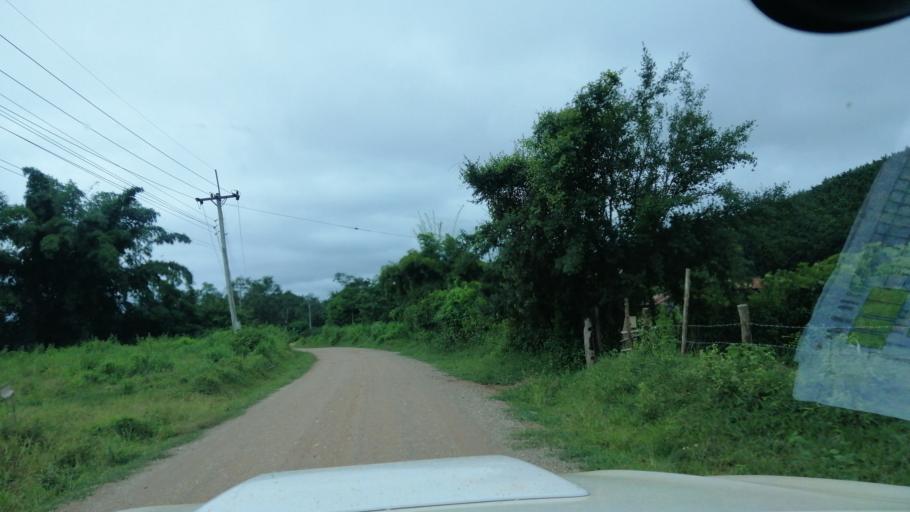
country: LA
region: Xiagnabouli
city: Muang Kenthao
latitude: 17.9567
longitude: 101.4079
